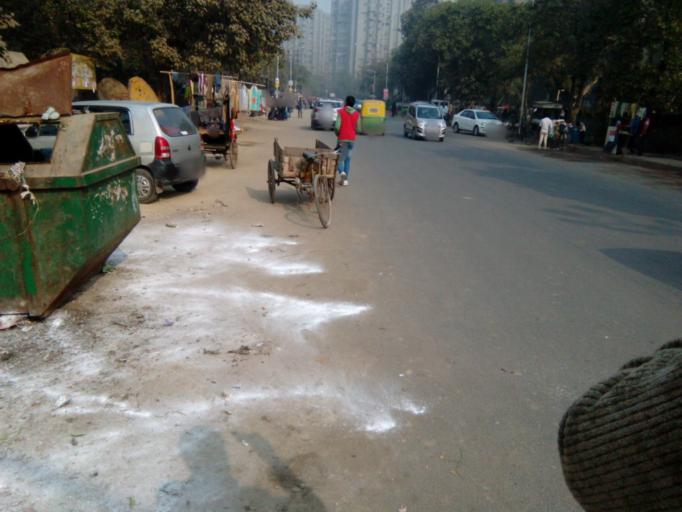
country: IN
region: Uttar Pradesh
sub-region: Gautam Buddha Nagar
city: Noida
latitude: 28.6412
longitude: 77.3195
